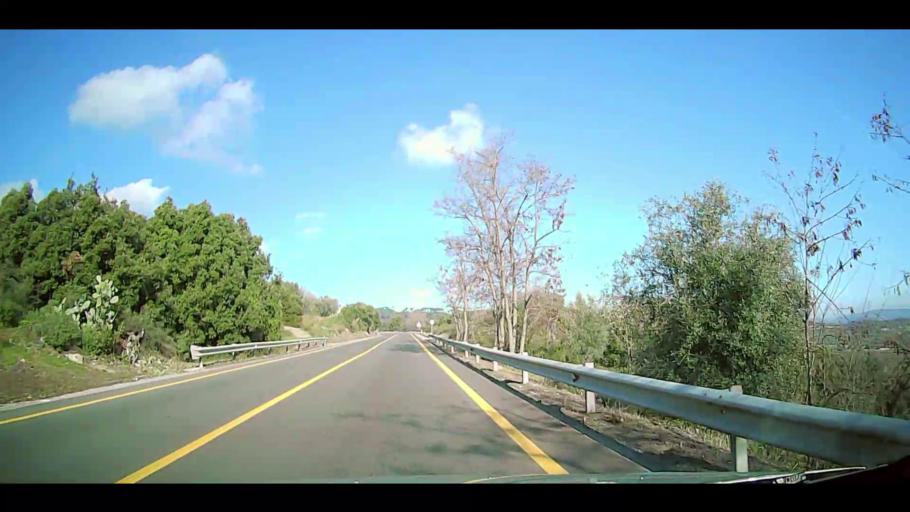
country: IT
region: Calabria
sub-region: Provincia di Crotone
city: Caccuri
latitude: 39.2291
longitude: 16.7947
